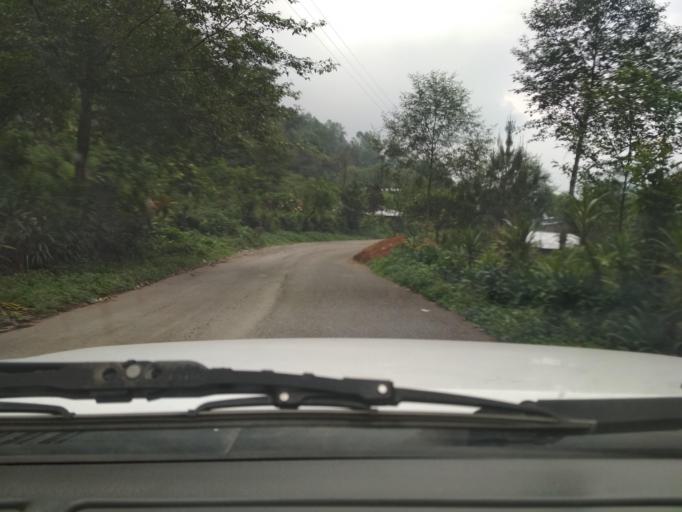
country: MX
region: Veracruz
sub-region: La Perla
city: Barrio de San Miguel
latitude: 18.9479
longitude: -97.1347
